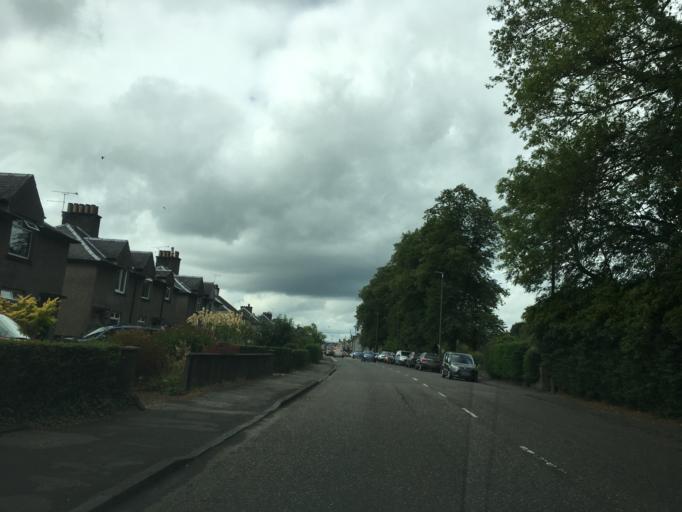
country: GB
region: Scotland
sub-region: Stirling
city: Stirling
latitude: 56.1367
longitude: -3.9194
